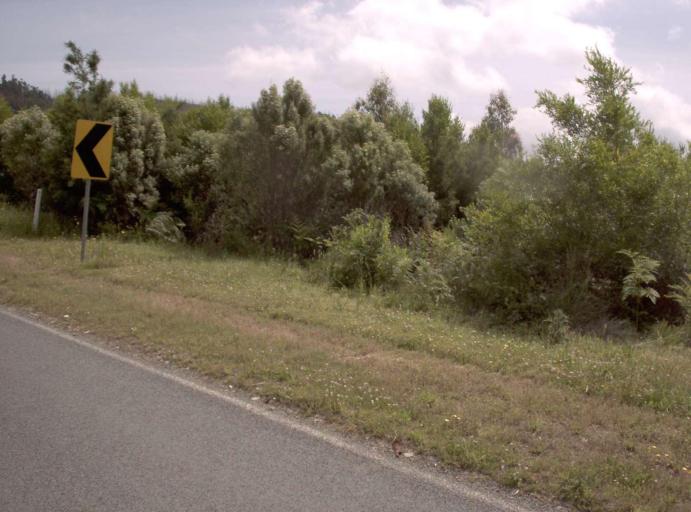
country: AU
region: Victoria
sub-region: Latrobe
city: Traralgon
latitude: -38.3836
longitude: 146.5665
